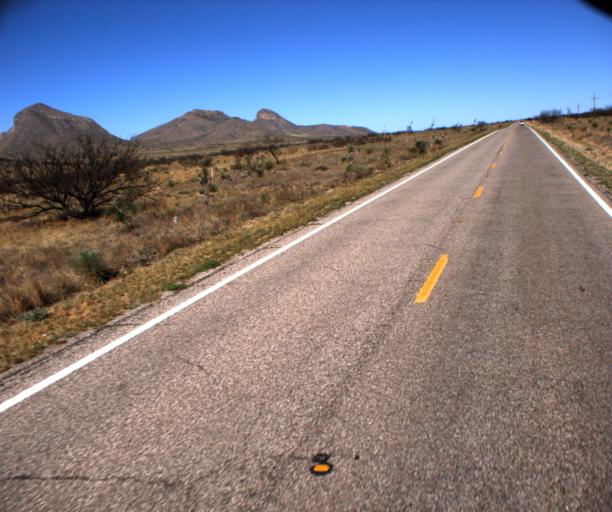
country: US
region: Arizona
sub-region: Cochise County
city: Huachuca City
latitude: 31.7016
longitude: -110.4314
